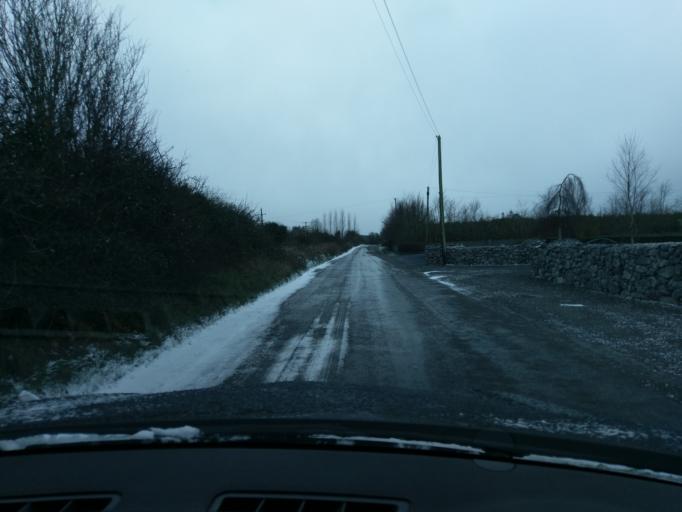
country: IE
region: Connaught
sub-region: County Galway
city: Athenry
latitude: 53.2759
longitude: -8.8063
